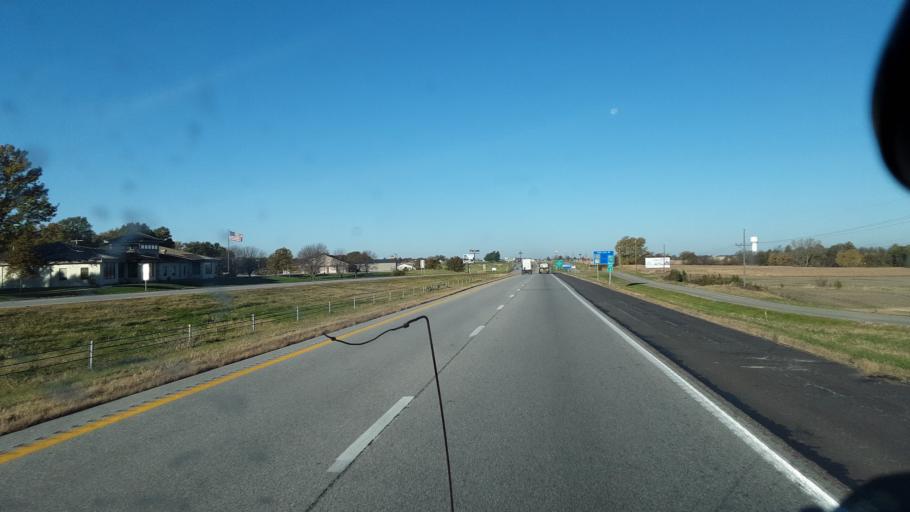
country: US
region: Missouri
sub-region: Lafayette County
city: Concordia
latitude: 38.9898
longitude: -93.5528
